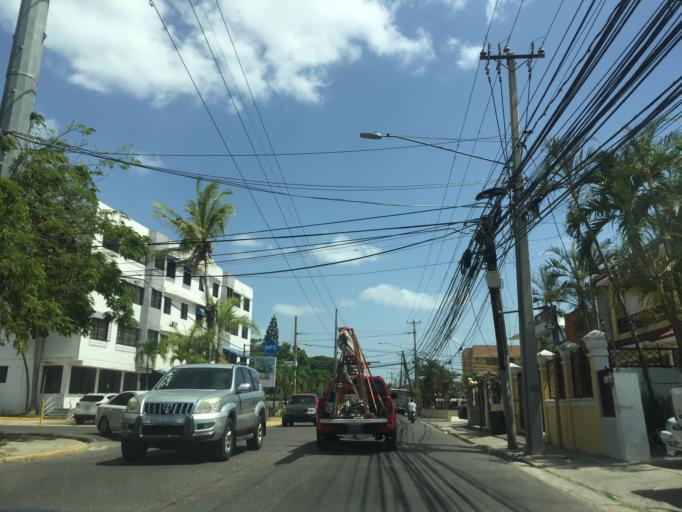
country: DO
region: Santiago
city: Santiago de los Caballeros
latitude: 19.4516
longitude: -70.6657
